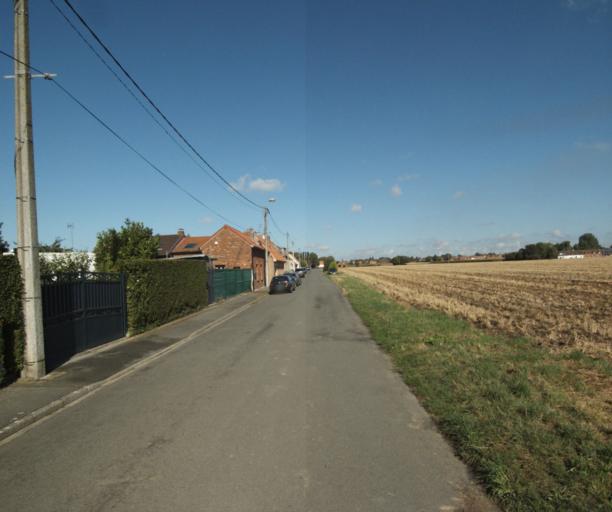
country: FR
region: Nord-Pas-de-Calais
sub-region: Departement du Nord
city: Toufflers
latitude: 50.6519
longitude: 3.2444
